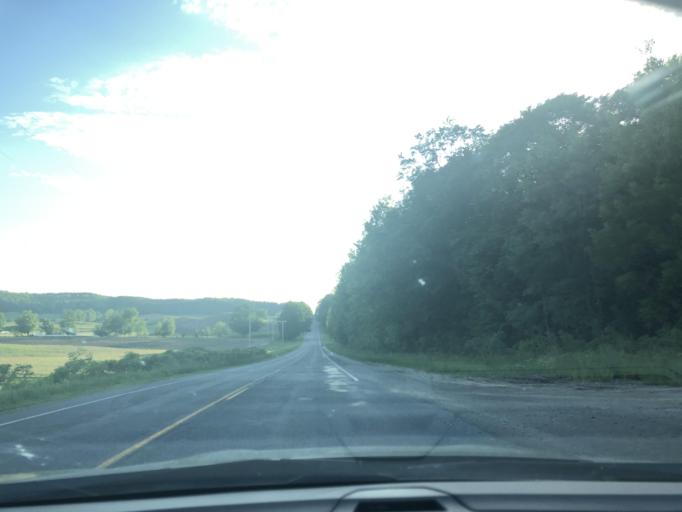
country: US
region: Michigan
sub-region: Missaukee County
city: Lake City
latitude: 44.4667
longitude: -85.0942
